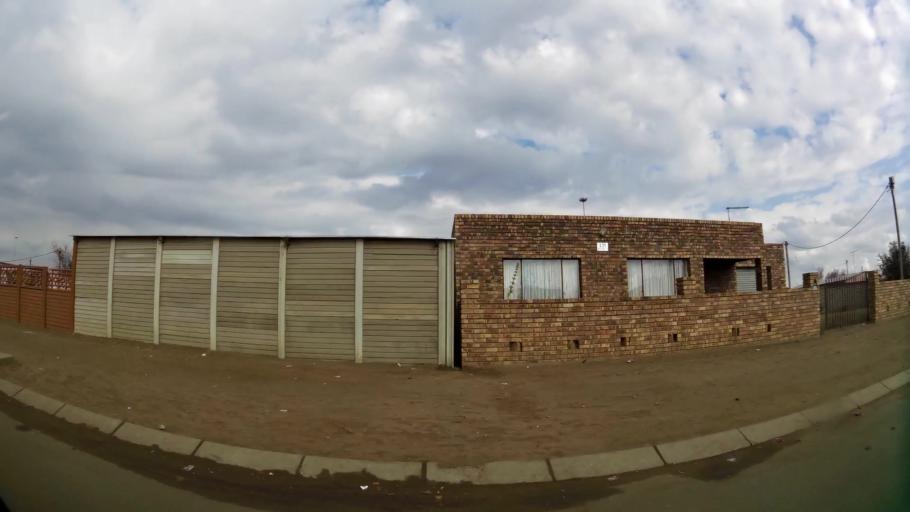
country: ZA
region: Gauteng
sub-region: Sedibeng District Municipality
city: Vanderbijlpark
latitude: -26.6960
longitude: 27.7924
